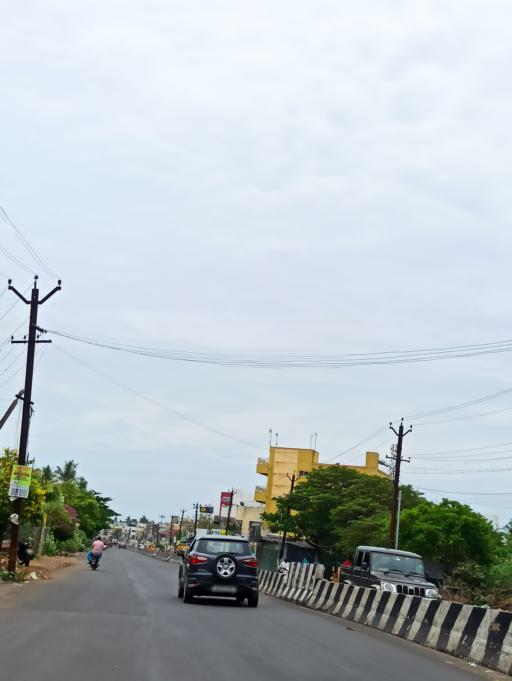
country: IN
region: Tamil Nadu
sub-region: Kancheepuram
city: Vandalur
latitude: 12.9211
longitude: 80.0901
